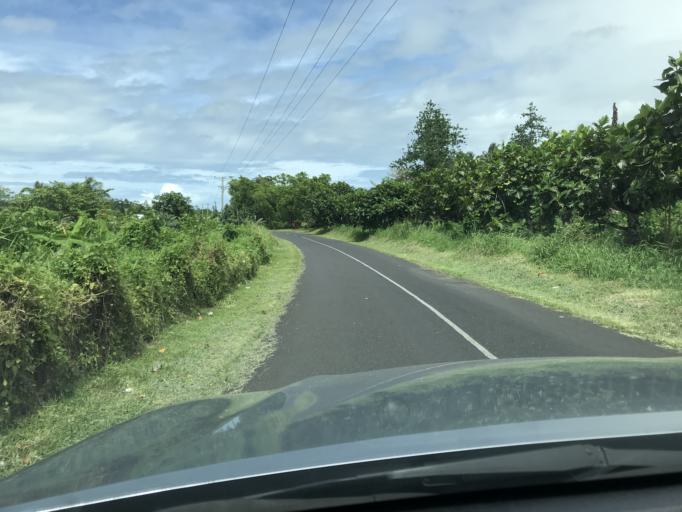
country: WS
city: Fasito`outa
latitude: -13.8588
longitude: -171.9050
